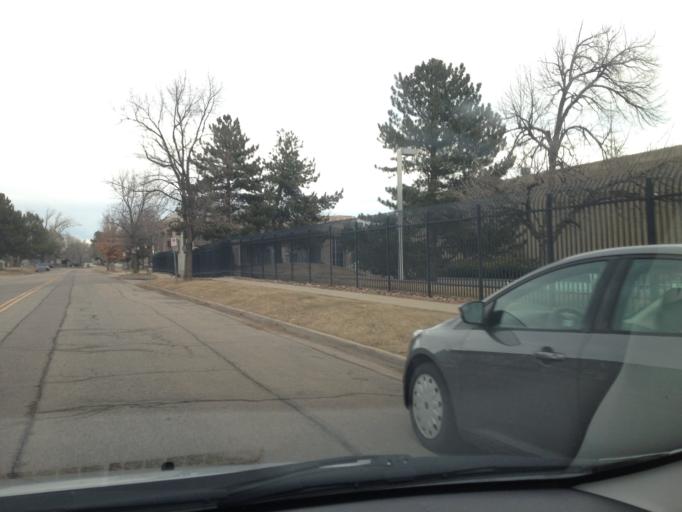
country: US
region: Colorado
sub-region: Boulder County
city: Boulder
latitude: 40.0164
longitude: -105.2500
